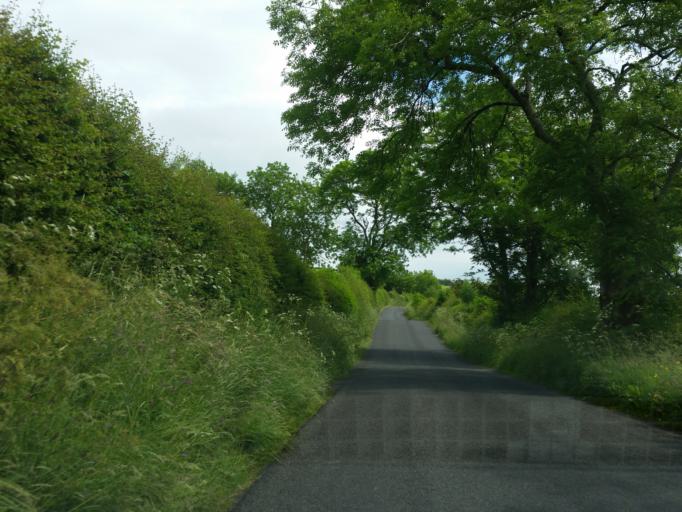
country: GB
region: Northern Ireland
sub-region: Omagh District
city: Omagh
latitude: 54.5485
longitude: -7.0895
